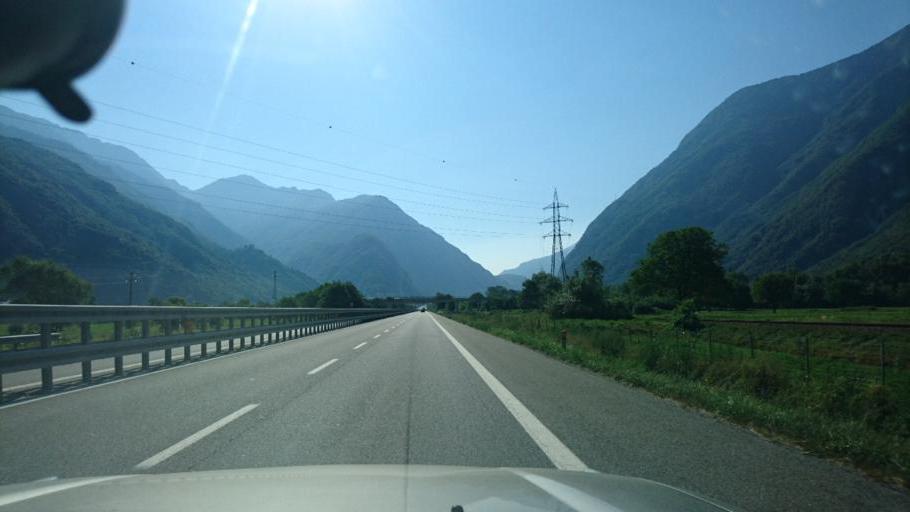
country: IT
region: Aosta Valley
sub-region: Valle d'Aosta
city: Arnad
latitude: 45.6521
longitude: 7.7020
